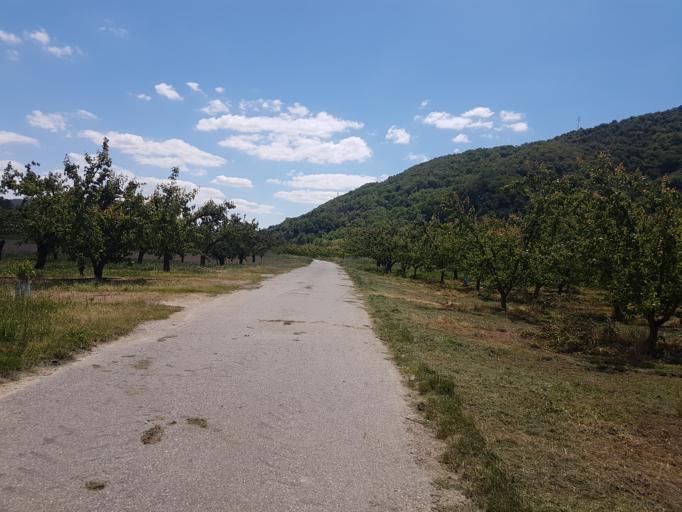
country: FR
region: Rhone-Alpes
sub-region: Departement de l'Ardeche
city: Saint-Jean-de-Muzols
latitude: 45.1112
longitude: 4.8122
